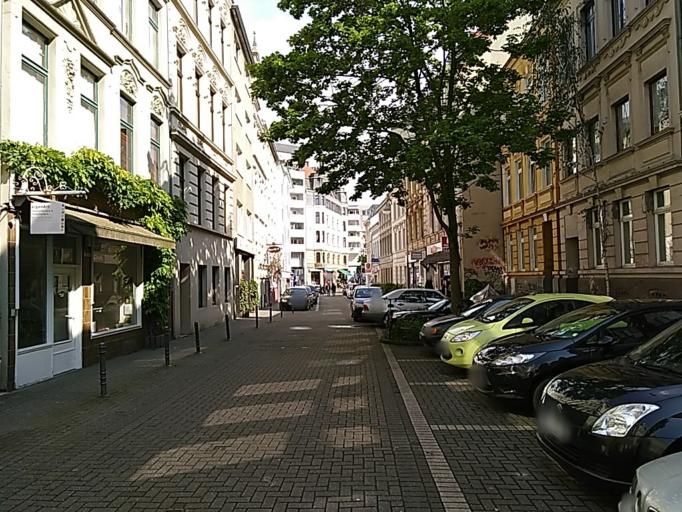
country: DE
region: North Rhine-Westphalia
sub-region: Regierungsbezirk Koln
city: Nippes
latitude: 50.9658
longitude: 6.9524
